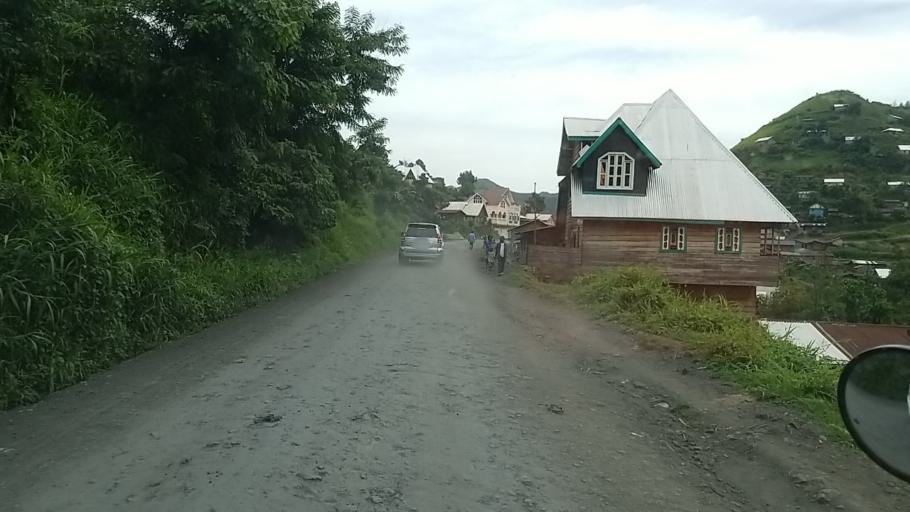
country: CD
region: Nord Kivu
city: Sake
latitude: -1.7547
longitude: 28.9856
